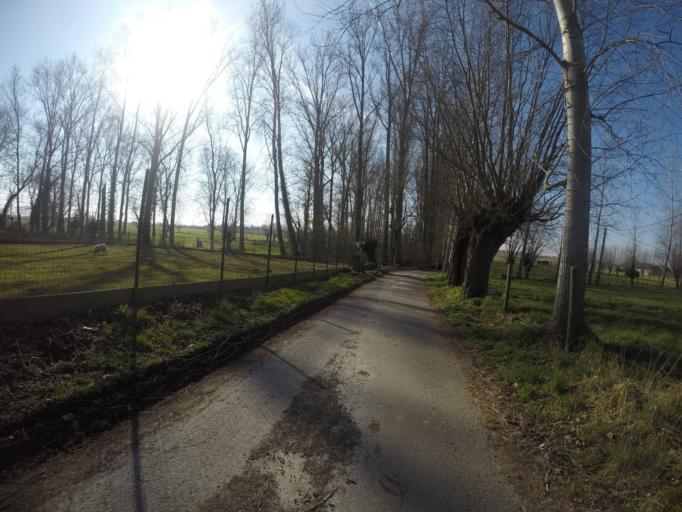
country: BE
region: Flanders
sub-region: Provincie Oost-Vlaanderen
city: Sint-Maria-Lierde
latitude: 50.8079
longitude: 3.8045
